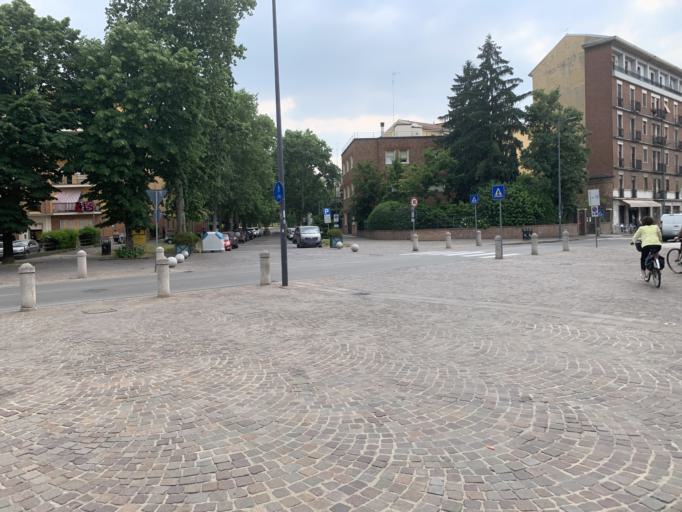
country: IT
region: Emilia-Romagna
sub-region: Provincia di Piacenza
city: Piacenza
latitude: 45.0463
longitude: 9.7034
